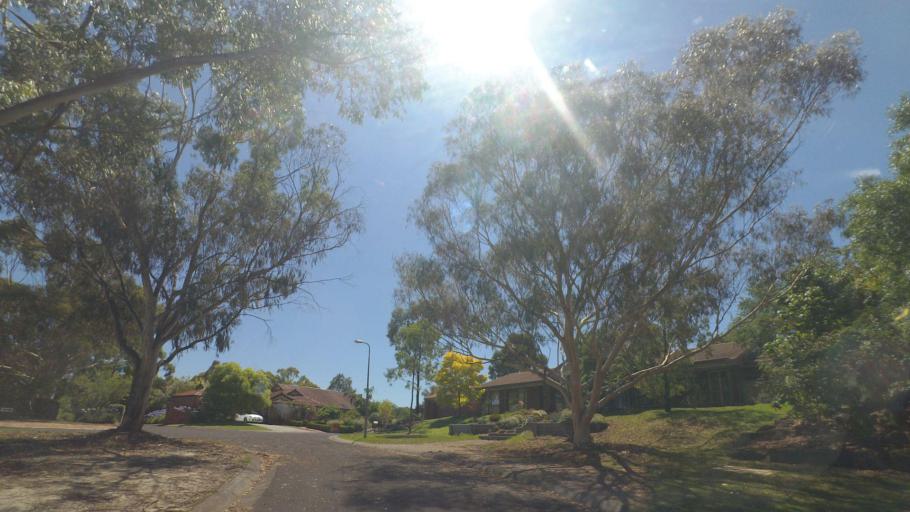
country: AU
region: Victoria
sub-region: Maroondah
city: Warranwood
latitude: -37.7808
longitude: 145.2407
